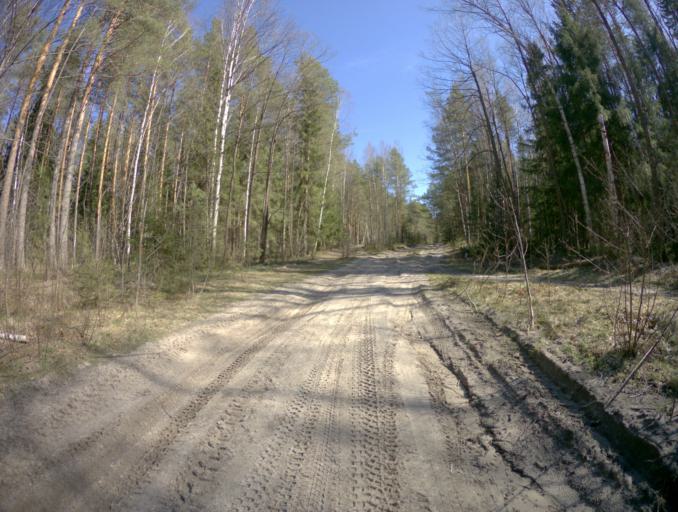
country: RU
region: Vladimir
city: Ivanishchi
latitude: 55.7929
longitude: 40.4241
